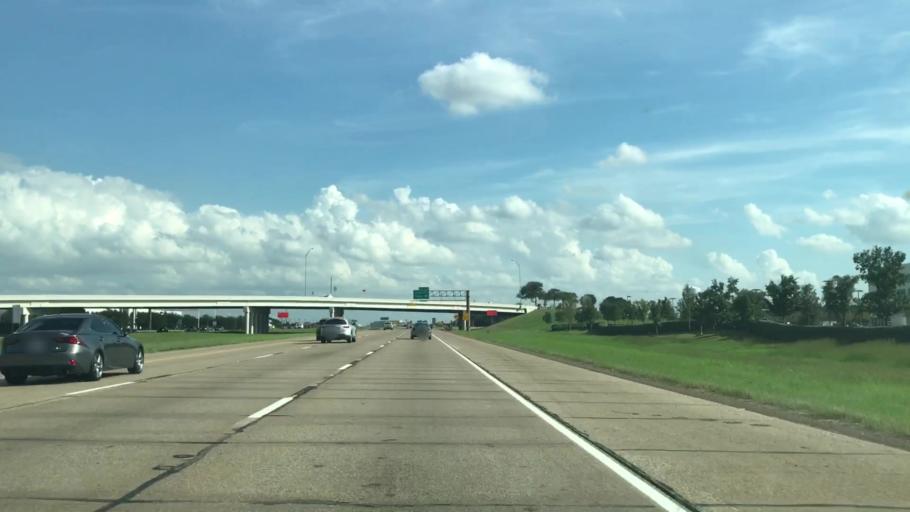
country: US
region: Texas
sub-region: Dallas County
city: Coppell
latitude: 32.9364
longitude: -97.0098
